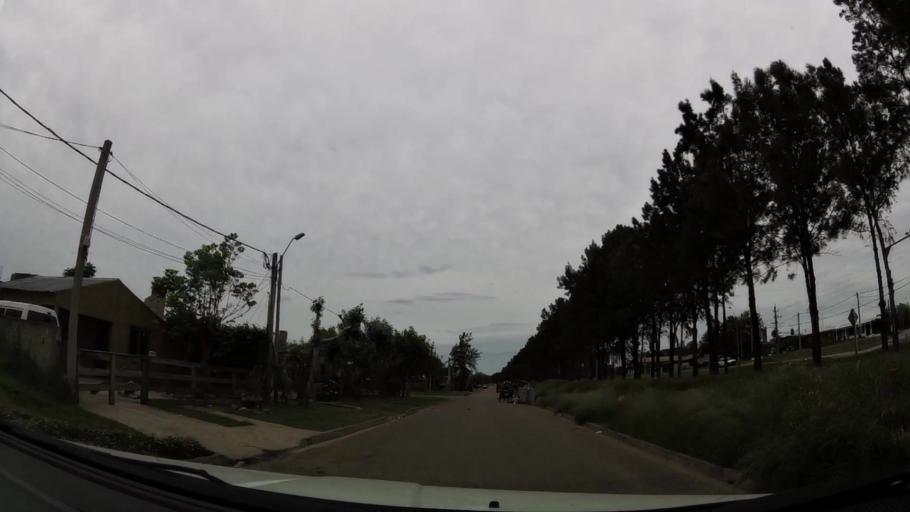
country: UY
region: Maldonado
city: Maldonado
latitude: -34.8798
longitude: -54.9814
